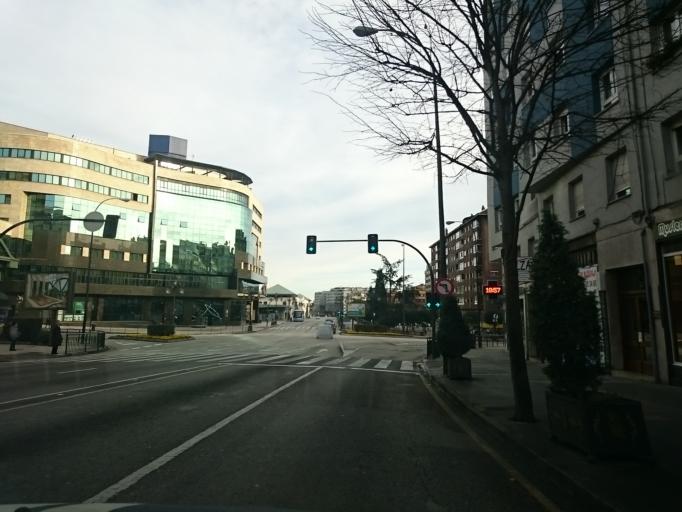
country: ES
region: Asturias
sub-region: Province of Asturias
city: Oviedo
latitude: 43.3643
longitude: -5.8393
